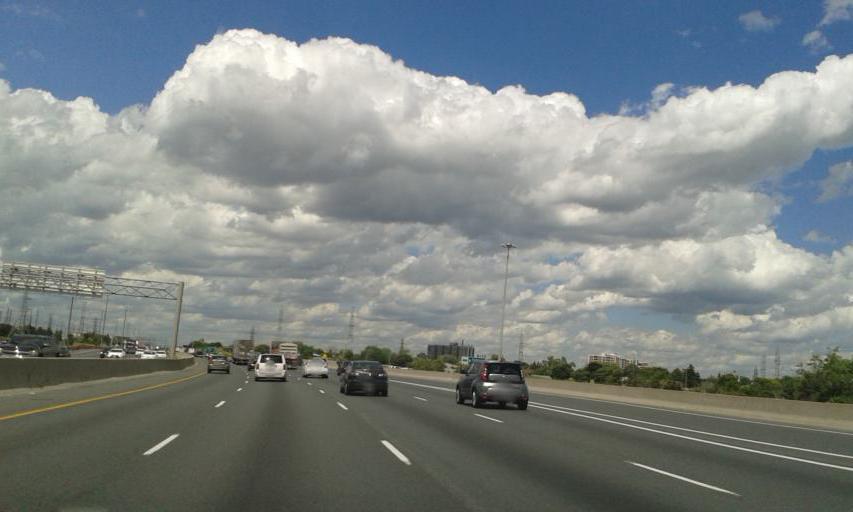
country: CA
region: Ontario
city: Etobicoke
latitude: 43.6746
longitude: -79.5790
